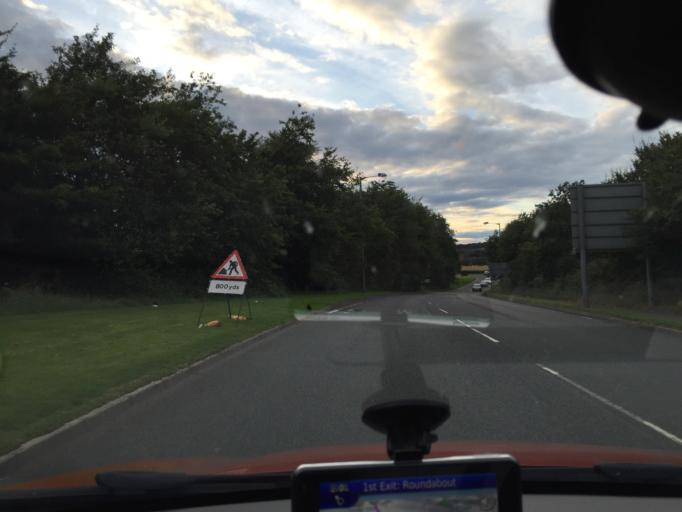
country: GB
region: Scotland
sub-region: Falkirk
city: Larbert
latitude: 56.0077
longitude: -3.8403
